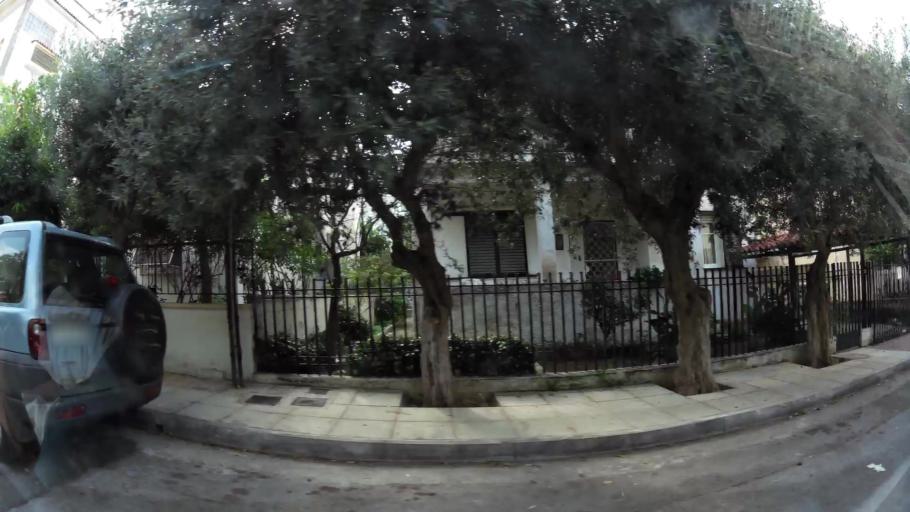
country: GR
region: Attica
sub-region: Nomarchia Athinas
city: Cholargos
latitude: 37.9998
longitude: 23.8055
